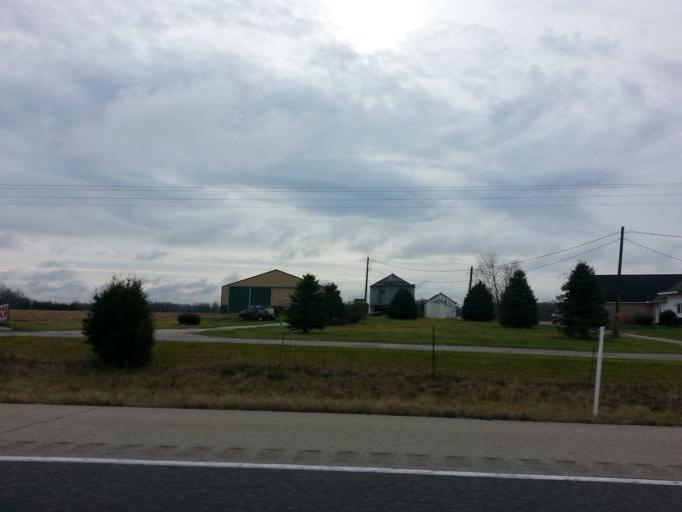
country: US
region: Indiana
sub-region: Ripley County
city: Batesville
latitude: 39.3168
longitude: -85.3102
